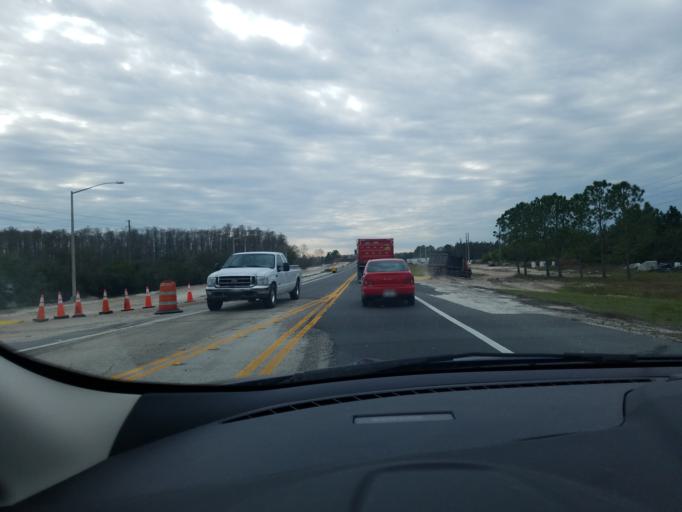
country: US
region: Florida
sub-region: Orange County
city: Meadow Woods
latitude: 28.3623
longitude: -81.3856
